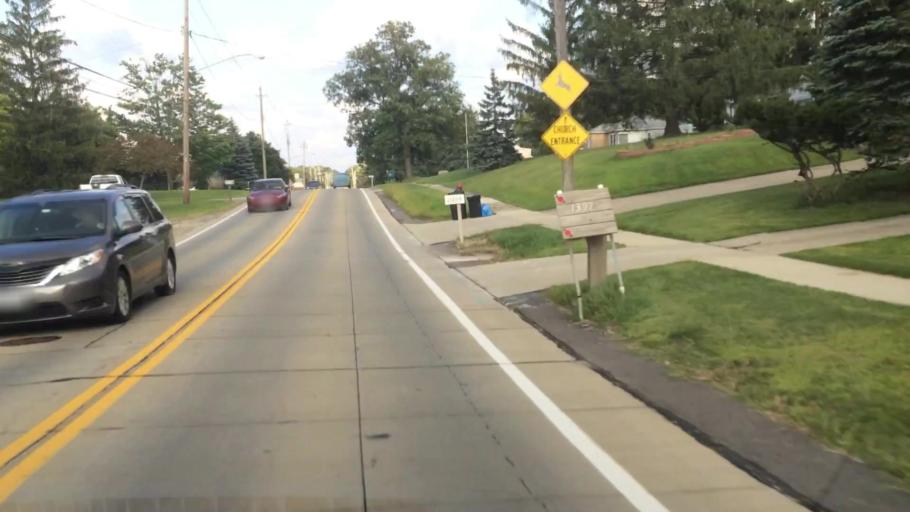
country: US
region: Ohio
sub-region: Cuyahoga County
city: Broadview Heights
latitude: 41.3509
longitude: -81.6905
